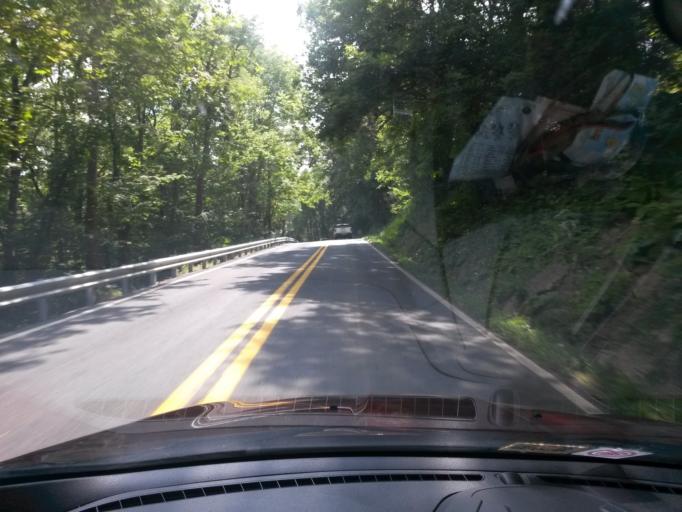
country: US
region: West Virginia
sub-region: Pendleton County
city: Franklin
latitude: 38.5664
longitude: -79.4255
